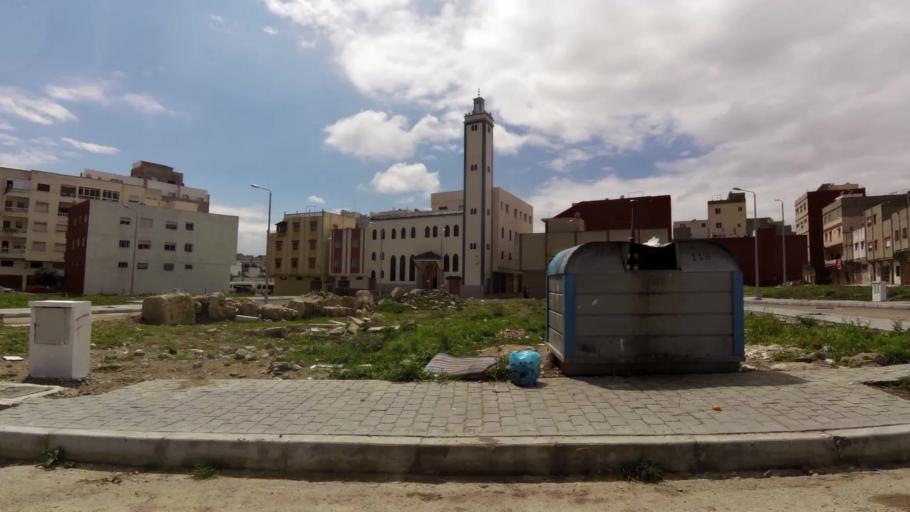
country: MA
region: Tanger-Tetouan
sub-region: Tanger-Assilah
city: Tangier
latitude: 35.7587
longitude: -5.8472
